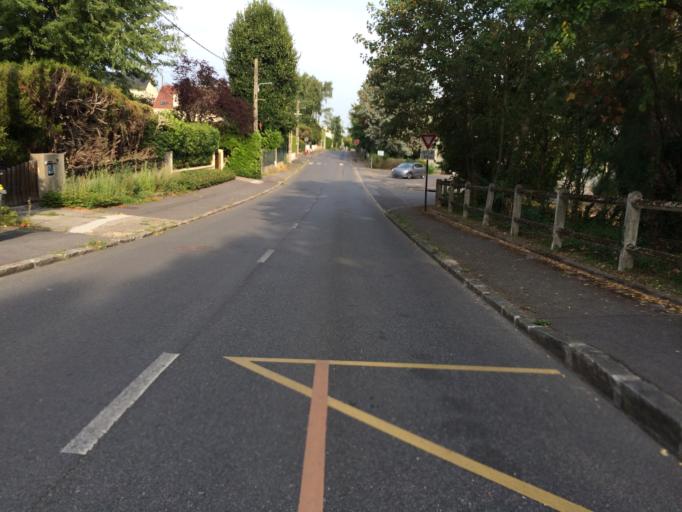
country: FR
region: Ile-de-France
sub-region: Departement de l'Essonne
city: Orsay
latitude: 48.7070
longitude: 2.1984
